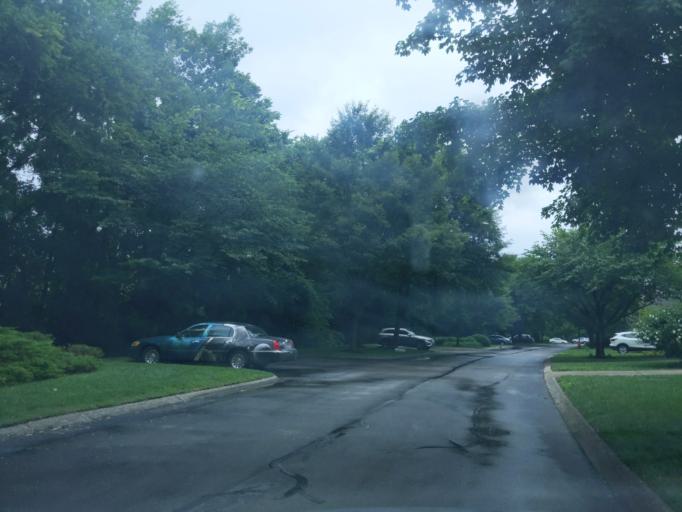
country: US
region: Tennessee
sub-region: Williamson County
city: Brentwood
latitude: 36.0392
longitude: -86.7592
